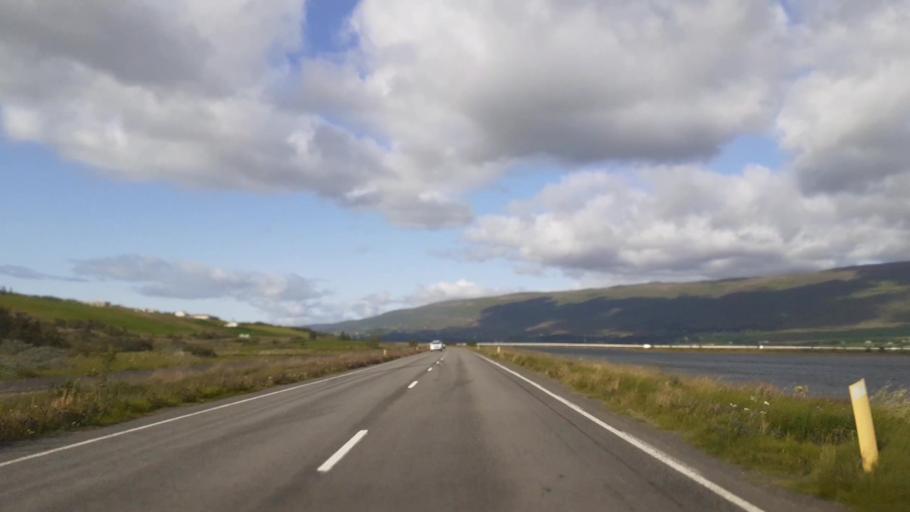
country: IS
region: Northeast
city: Akureyri
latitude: 65.6162
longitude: -18.0775
